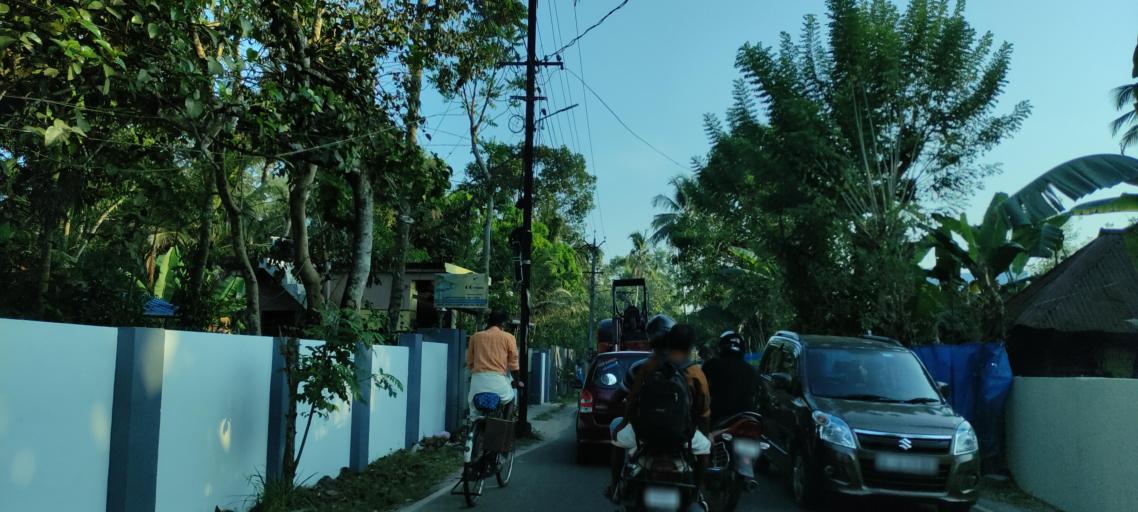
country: IN
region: Kerala
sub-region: Alappuzha
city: Shertallai
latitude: 9.6409
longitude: 76.3601
